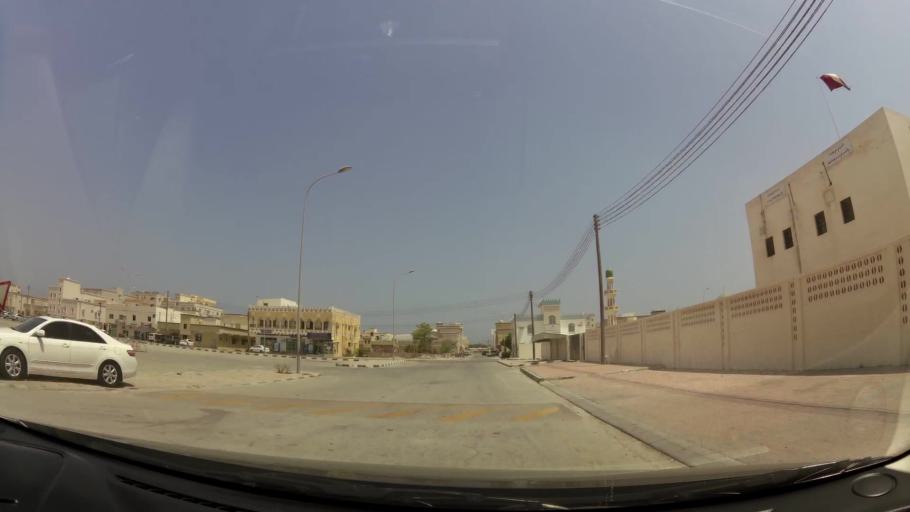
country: OM
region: Zufar
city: Salalah
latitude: 17.0148
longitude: 54.0768
